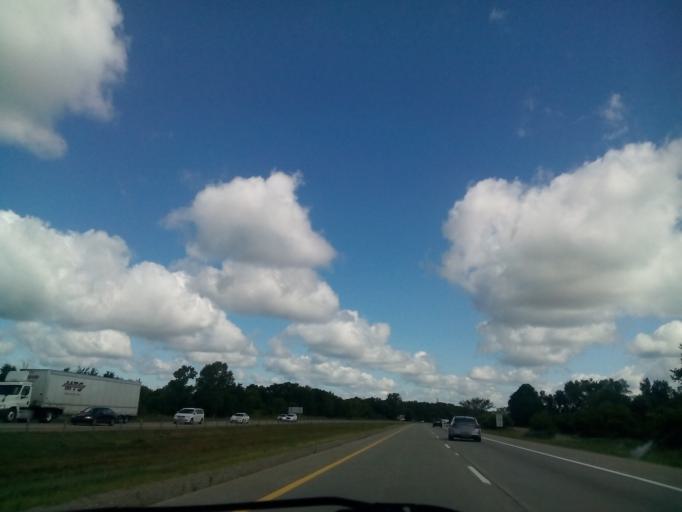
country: US
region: Michigan
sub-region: Genesee County
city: Linden
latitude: 42.7454
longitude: -83.7641
